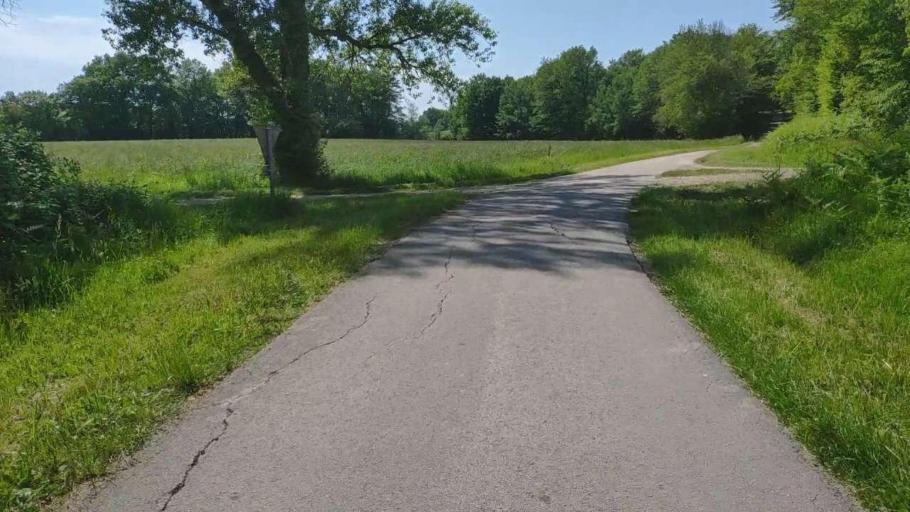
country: FR
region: Franche-Comte
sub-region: Departement du Jura
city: Bletterans
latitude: 46.8026
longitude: 5.4223
